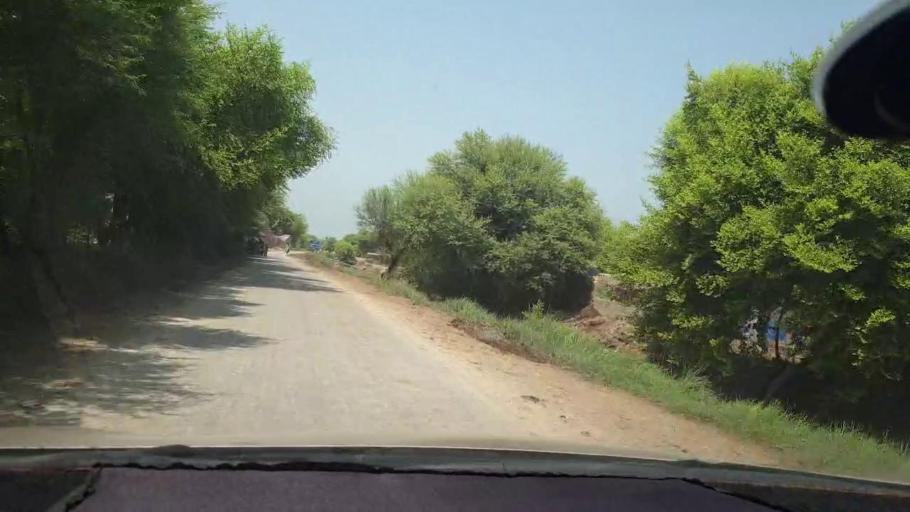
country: PK
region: Sindh
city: Kambar
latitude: 27.6495
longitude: 67.9676
